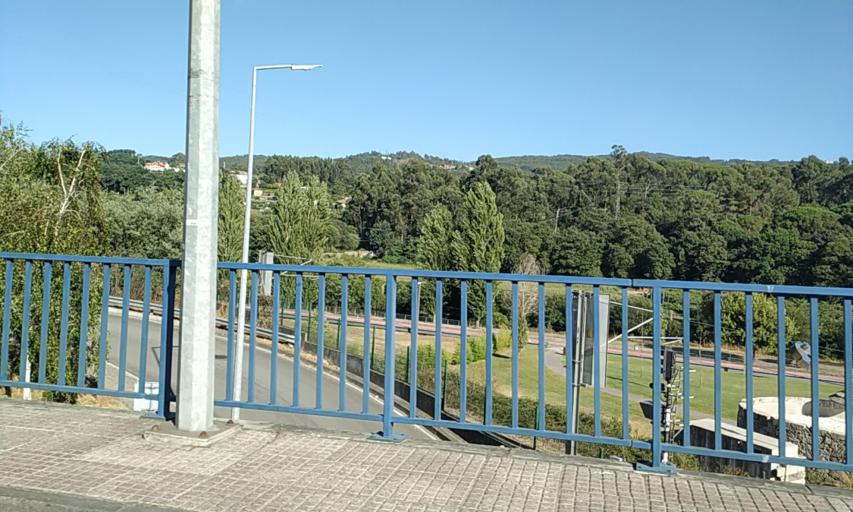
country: PT
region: Porto
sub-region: Santo Tirso
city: Santo Tirso
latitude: 41.3470
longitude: -8.4679
